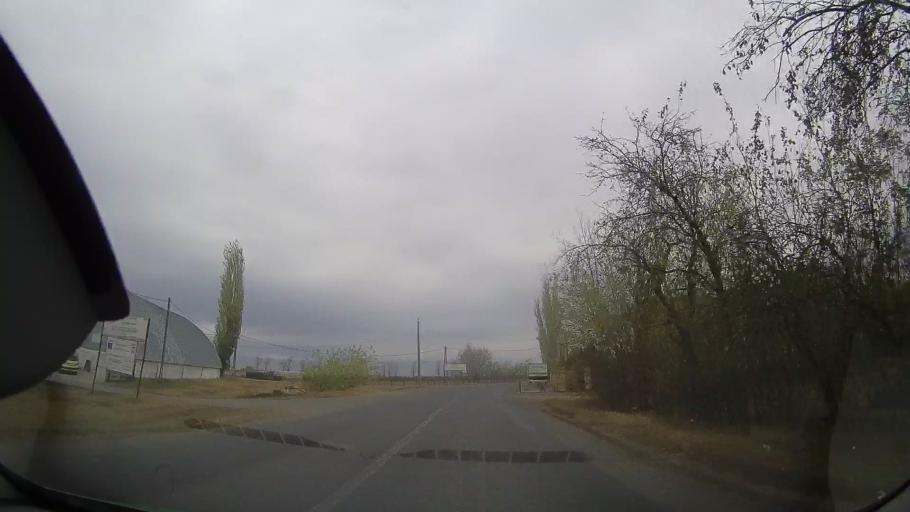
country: RO
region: Buzau
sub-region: Comuna Padina
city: Padina
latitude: 44.8211
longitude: 27.1178
